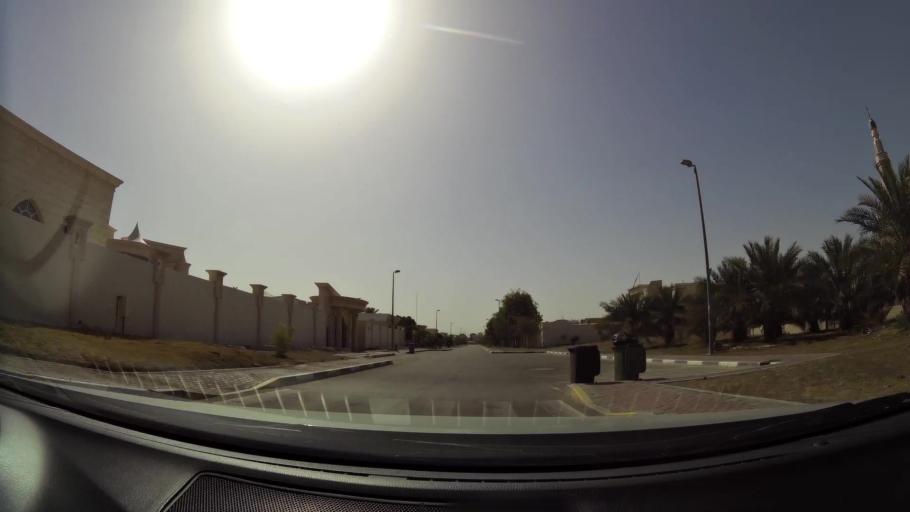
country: OM
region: Al Buraimi
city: Al Buraymi
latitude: 24.3389
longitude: 55.7957
